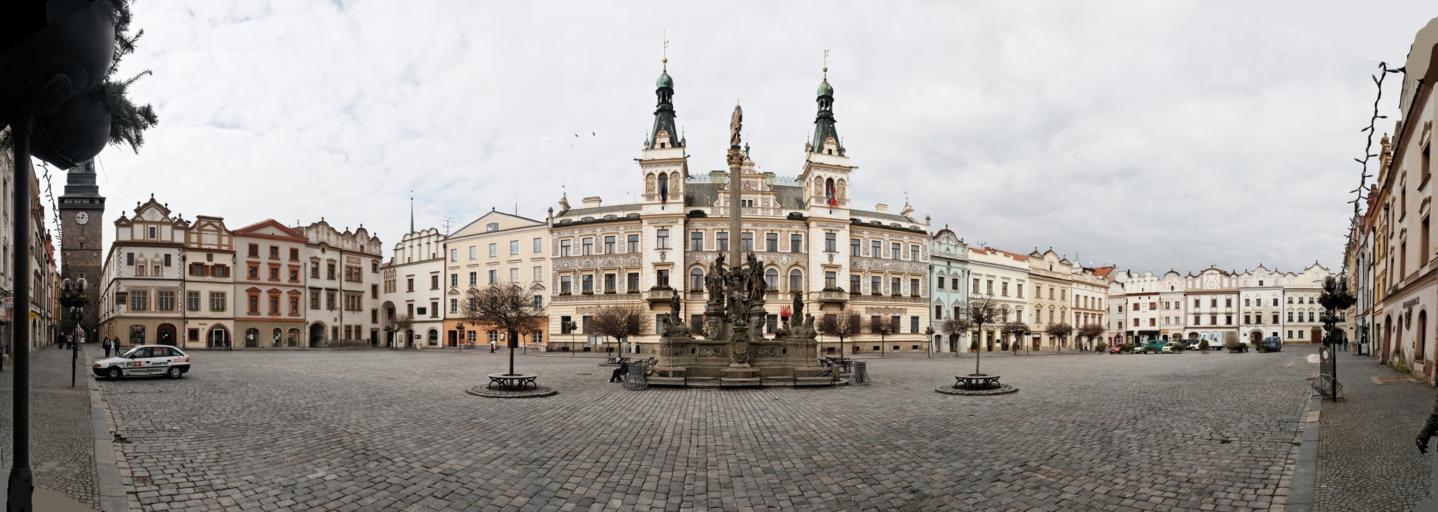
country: CZ
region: Pardubicky
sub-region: Okres Pardubice
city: Pardubice
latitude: 50.0386
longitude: 15.7792
